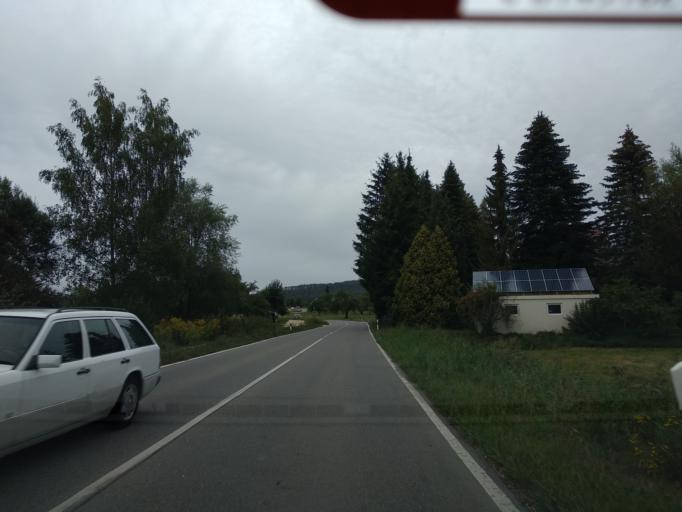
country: DE
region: Baden-Wuerttemberg
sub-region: Freiburg Region
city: Gottmadingen
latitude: 47.7253
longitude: 8.7552
